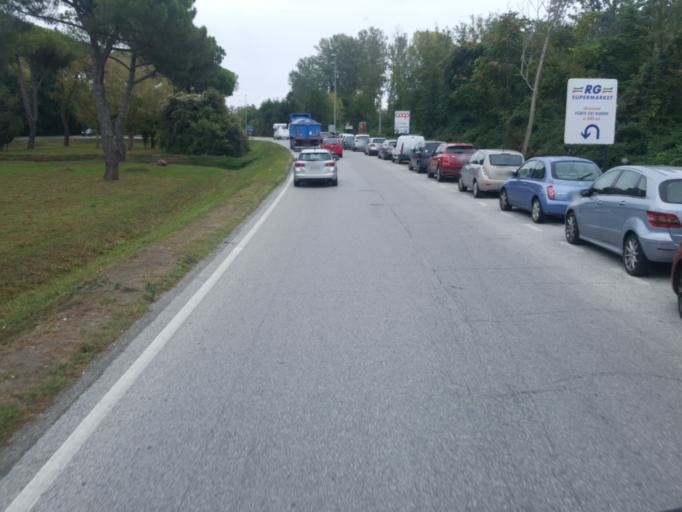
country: IT
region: Tuscany
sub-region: Provincia di Lucca
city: Forte dei Marmi
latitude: 43.9565
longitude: 10.1957
